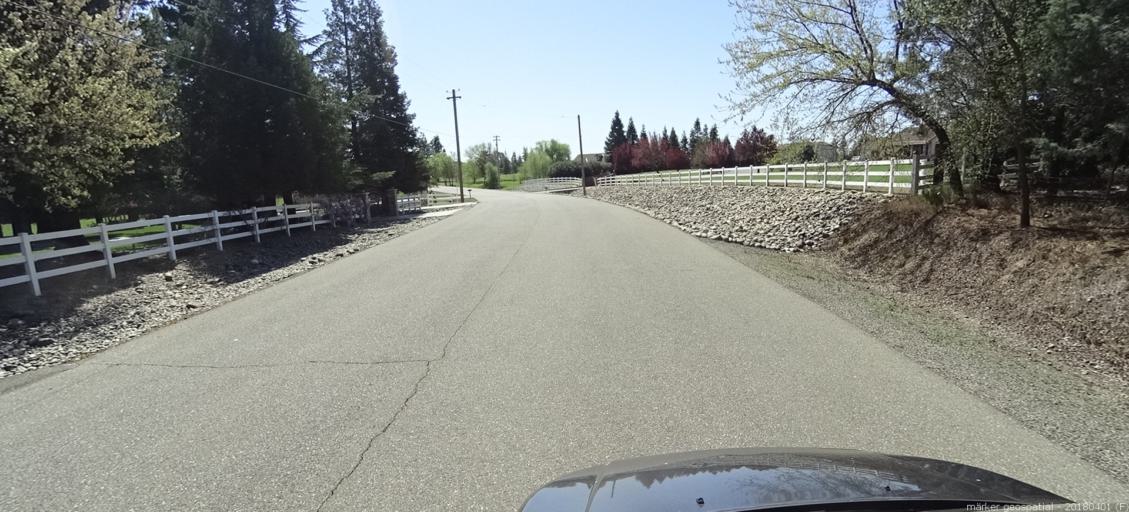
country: US
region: California
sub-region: Sacramento County
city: Wilton
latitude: 38.4158
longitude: -121.2276
